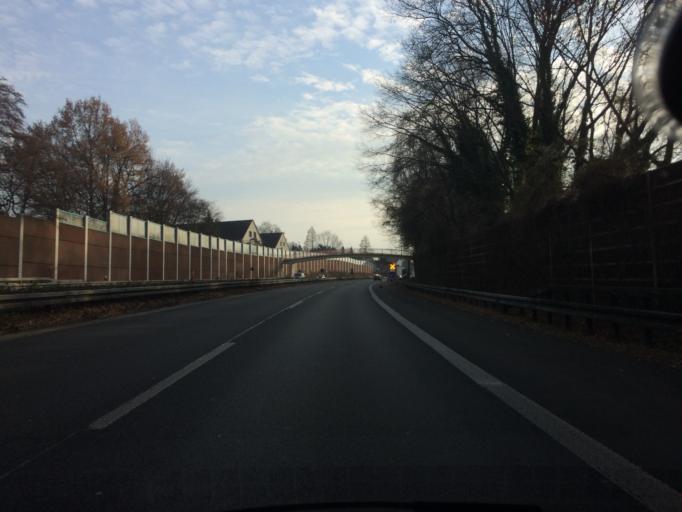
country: DE
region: North Rhine-Westphalia
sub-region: Regierungsbezirk Dusseldorf
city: Oberhausen
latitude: 51.5232
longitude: 6.8548
